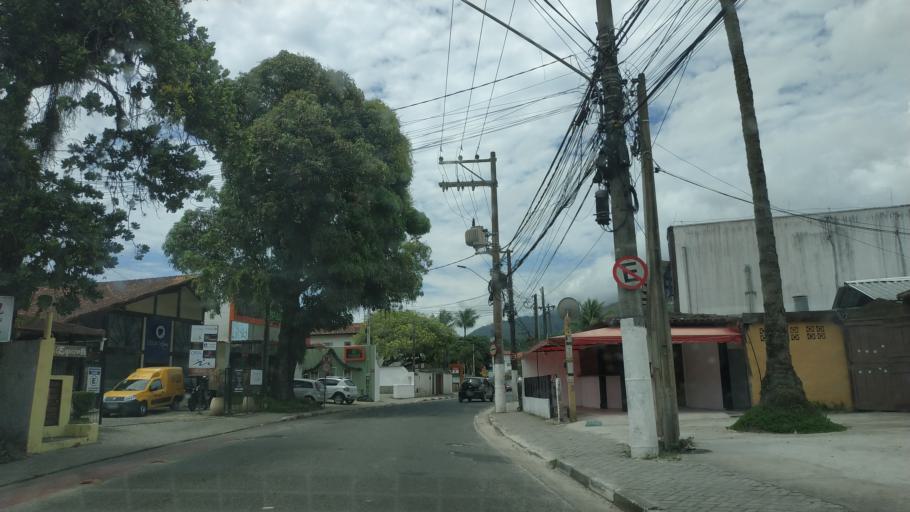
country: BR
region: Sao Paulo
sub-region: Ilhabela
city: Ilhabela
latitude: -23.8158
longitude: -45.3664
